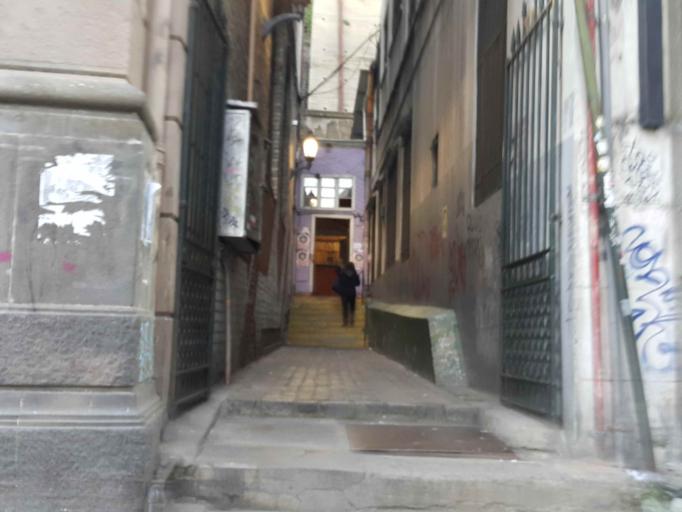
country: CL
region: Valparaiso
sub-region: Provincia de Valparaiso
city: Valparaiso
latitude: -33.0407
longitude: -71.6263
